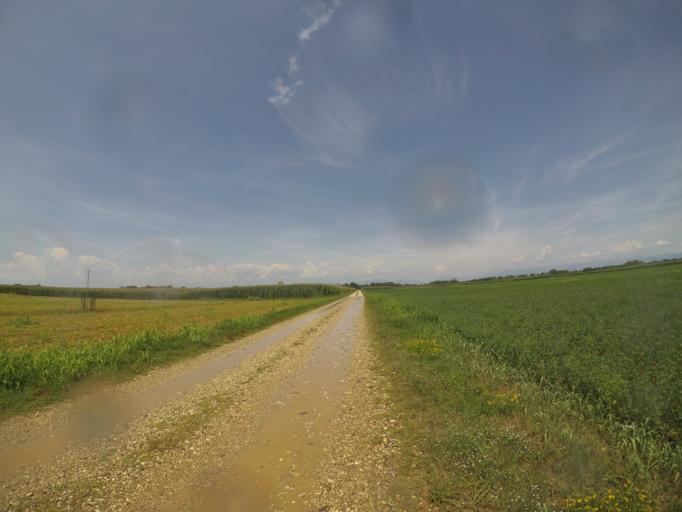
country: IT
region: Friuli Venezia Giulia
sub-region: Provincia di Udine
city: Lestizza
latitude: 45.9675
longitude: 13.0977
